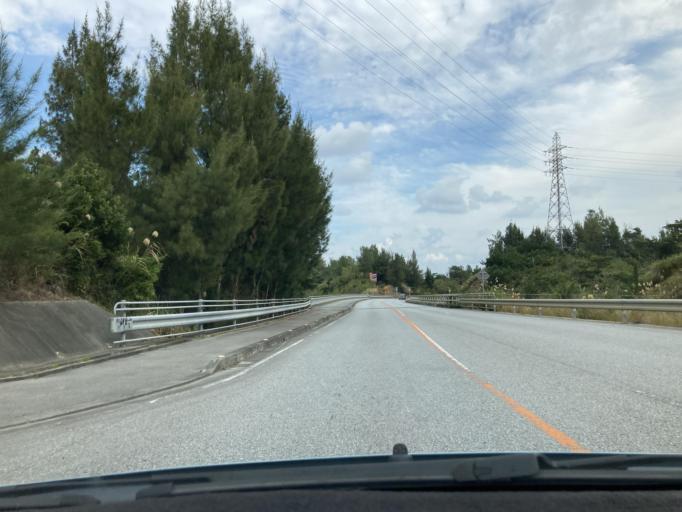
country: JP
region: Okinawa
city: Ishikawa
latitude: 26.5038
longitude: 127.8700
